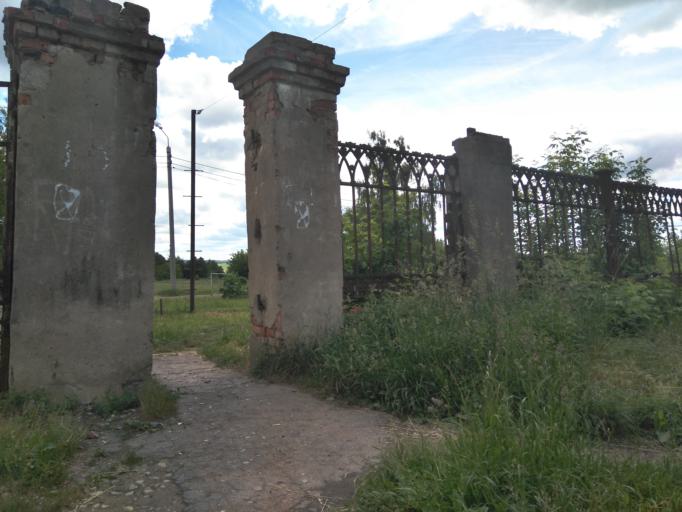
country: RU
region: Tula
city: Lomintsevskiy
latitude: 53.9300
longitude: 37.6244
